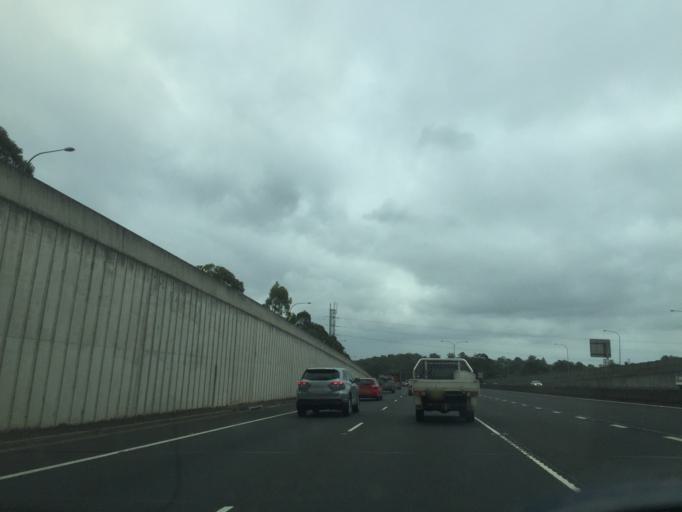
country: AU
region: New South Wales
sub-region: The Hills Shire
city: West Pennant
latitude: -33.7592
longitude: 151.0446
